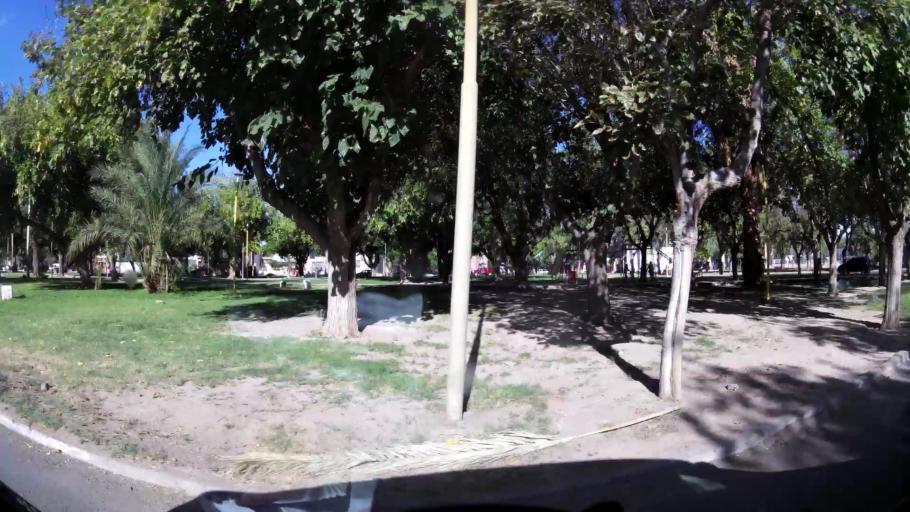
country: AR
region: San Juan
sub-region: Departamento de Santa Lucia
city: Santa Lucia
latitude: -31.5366
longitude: -68.5098
